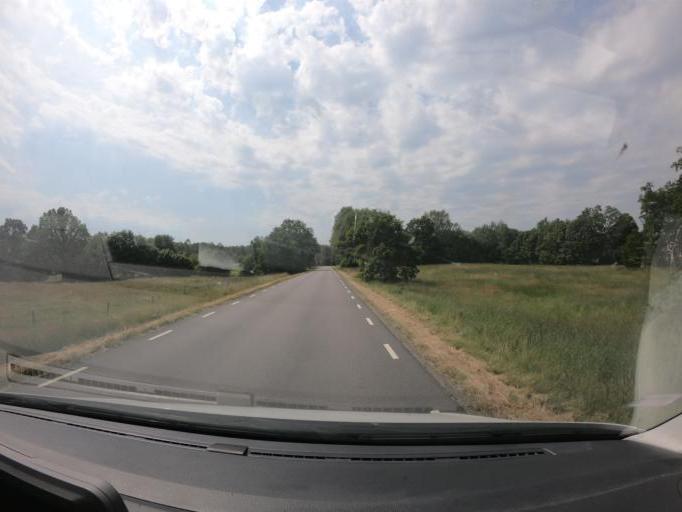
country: SE
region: Skane
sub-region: Hassleholms Kommun
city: Bjarnum
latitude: 56.2708
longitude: 13.5765
